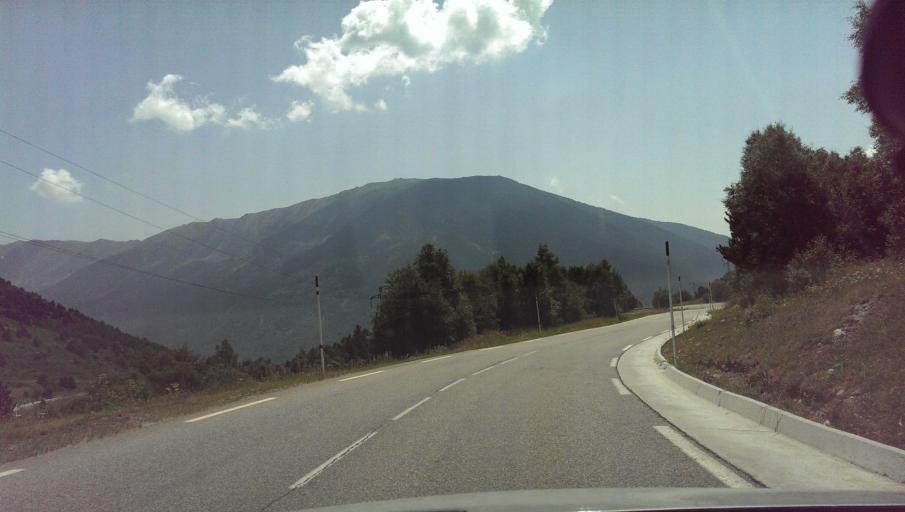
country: AD
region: Encamp
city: Pas de la Casa
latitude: 42.5541
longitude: 1.8153
